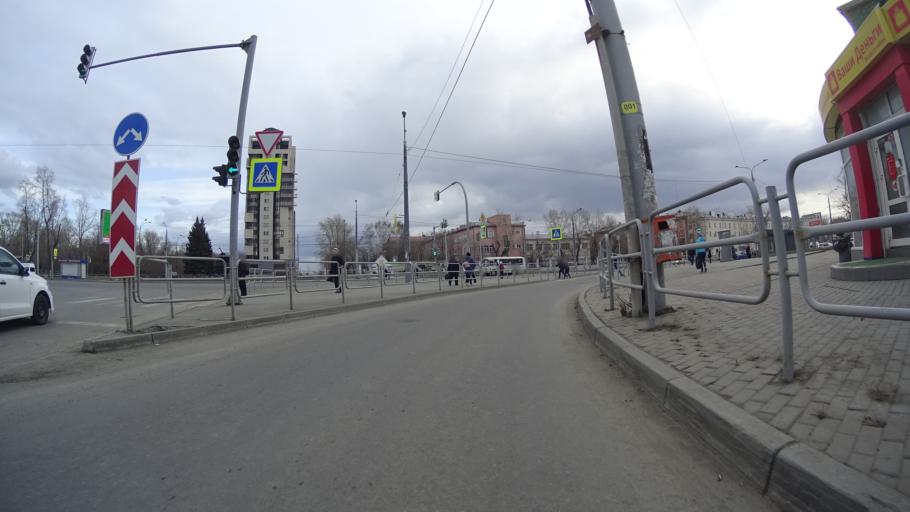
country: RU
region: Chelyabinsk
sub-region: Gorod Chelyabinsk
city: Chelyabinsk
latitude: 55.1611
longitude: 61.4412
